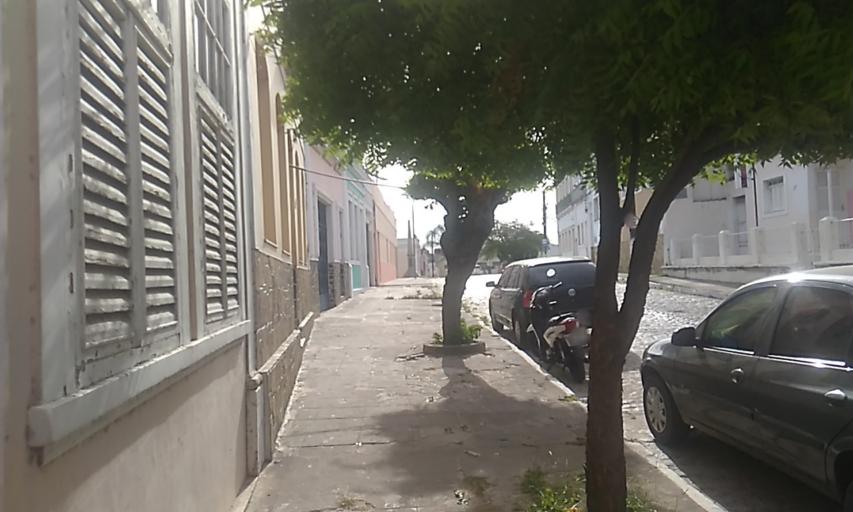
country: BR
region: Alagoas
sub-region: Penedo
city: Penedo
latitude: -10.2889
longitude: -36.5844
